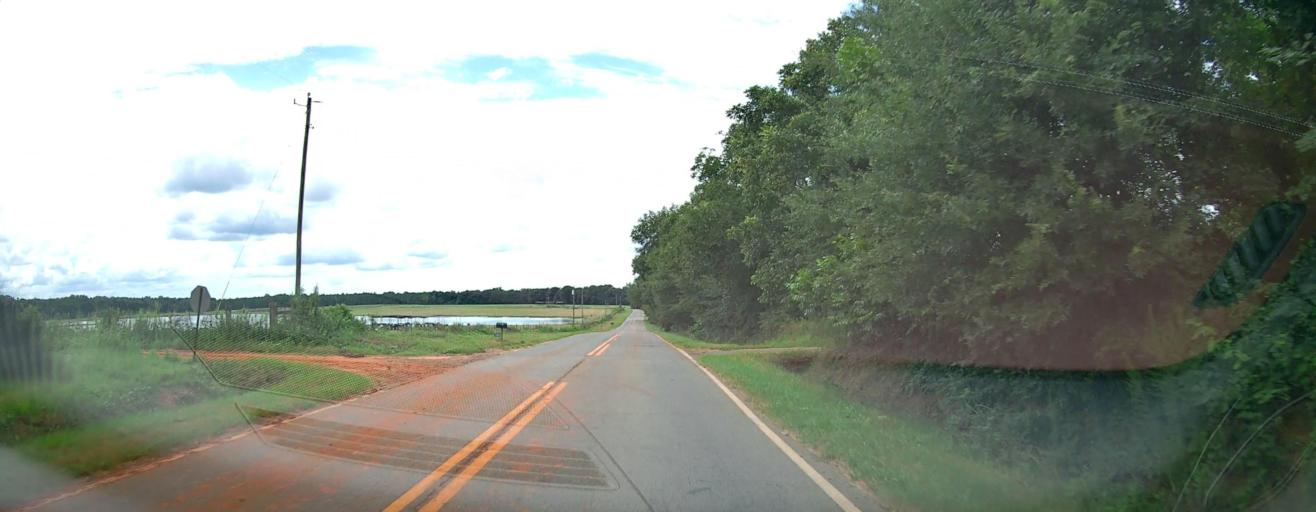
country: US
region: Georgia
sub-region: Macon County
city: Montezuma
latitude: 32.2917
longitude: -83.8828
